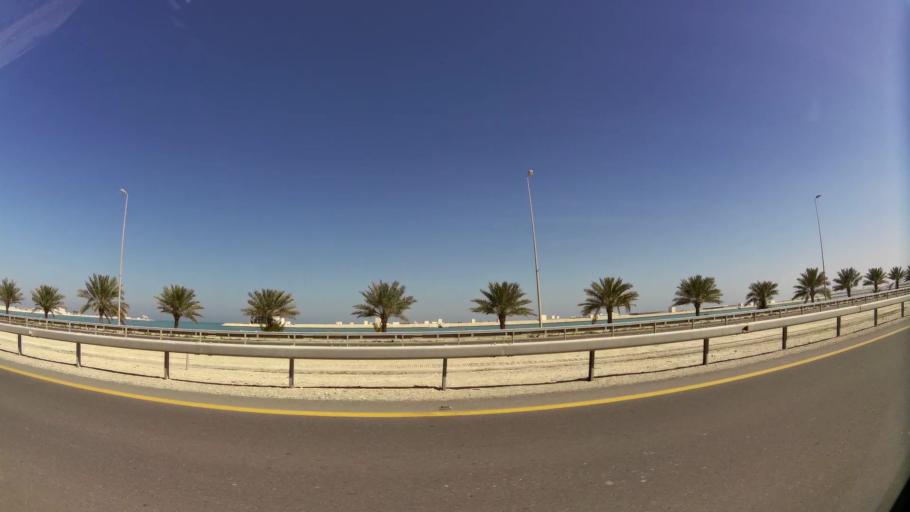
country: BH
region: Muharraq
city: Al Hadd
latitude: 26.2607
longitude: 50.6607
